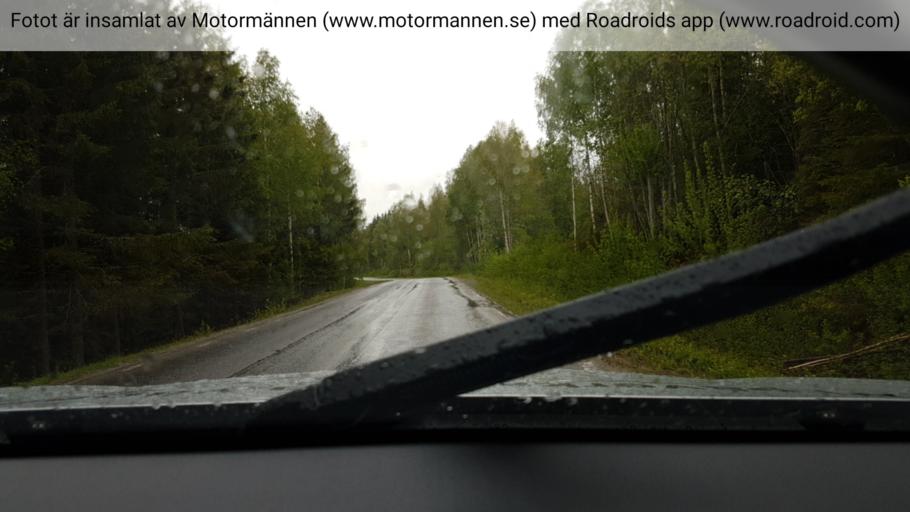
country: SE
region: Vaesterbotten
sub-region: Vannas Kommun
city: Vaennaes
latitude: 63.8679
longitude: 19.6691
